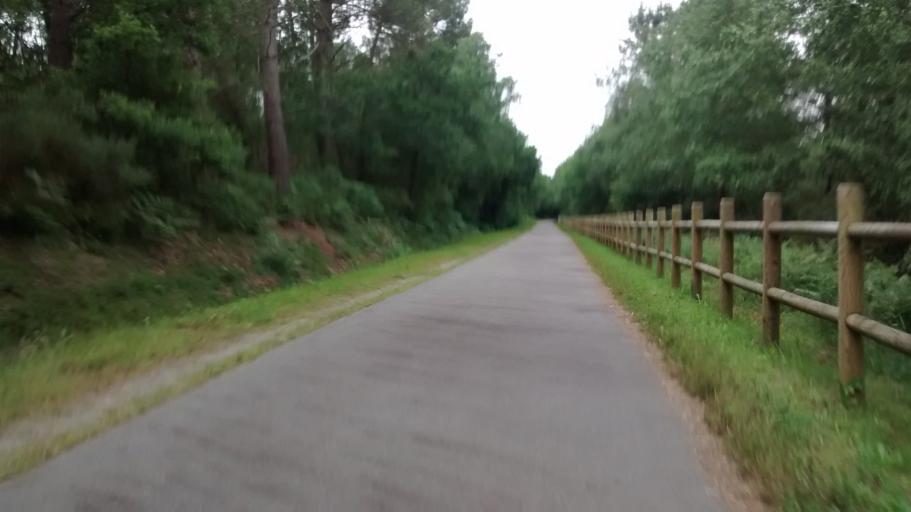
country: FR
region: Brittany
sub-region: Departement du Morbihan
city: Pleucadeuc
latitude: 47.7563
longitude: -2.4009
